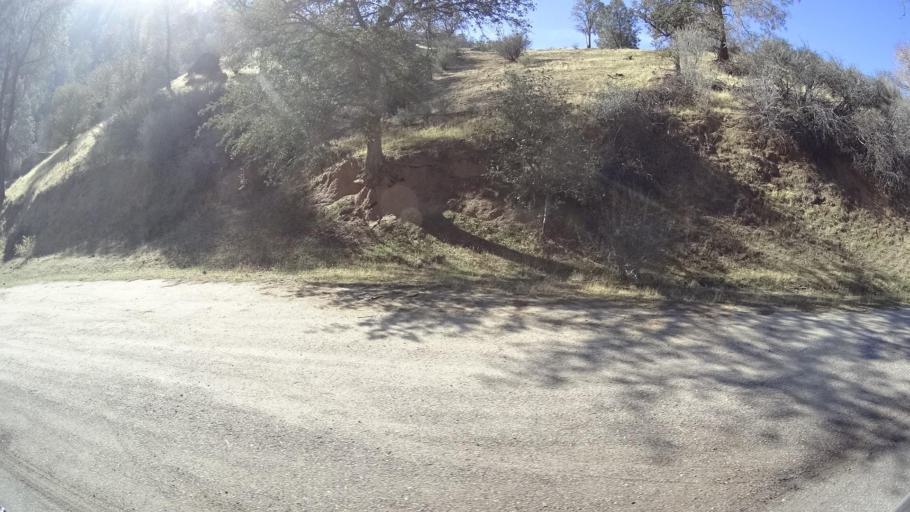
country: US
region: California
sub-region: Kern County
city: Bodfish
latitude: 35.5660
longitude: -118.5688
